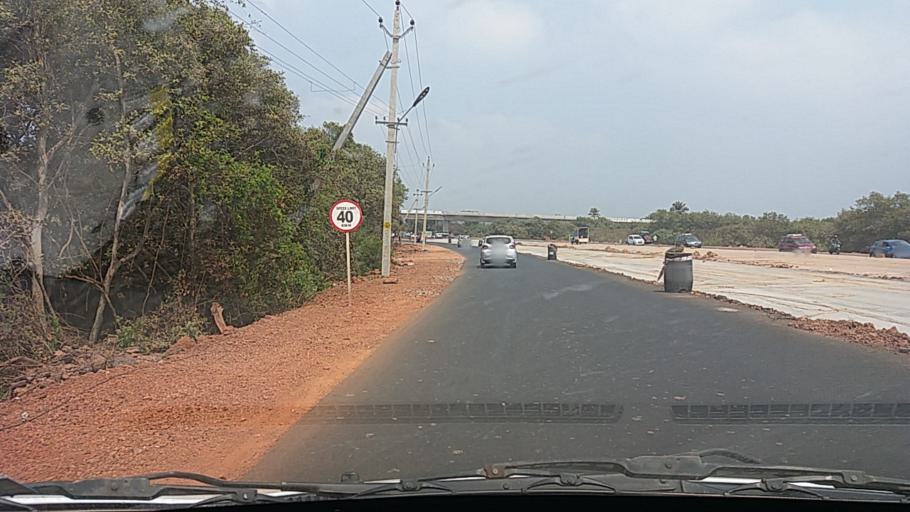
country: IN
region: Goa
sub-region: North Goa
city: Panaji
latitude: 15.4887
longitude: 73.8455
